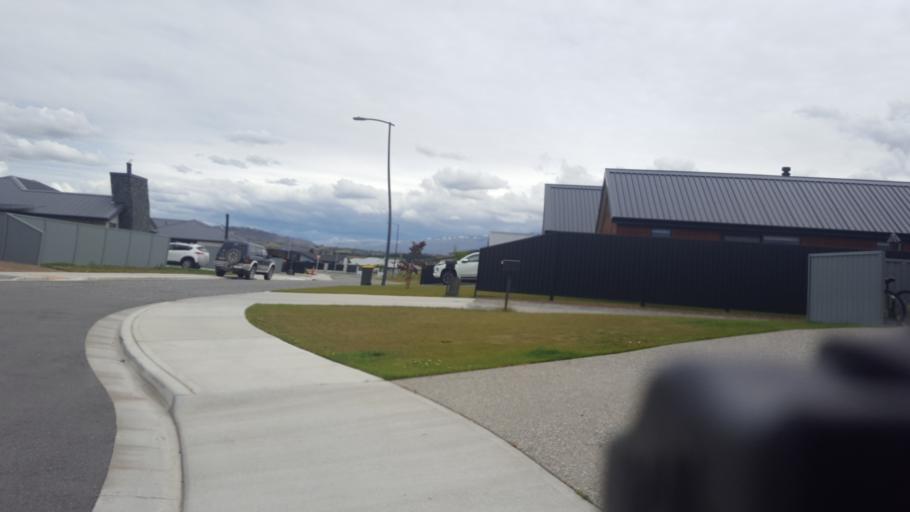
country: NZ
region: Otago
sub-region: Queenstown-Lakes District
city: Wanaka
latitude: -45.2420
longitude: 169.3755
